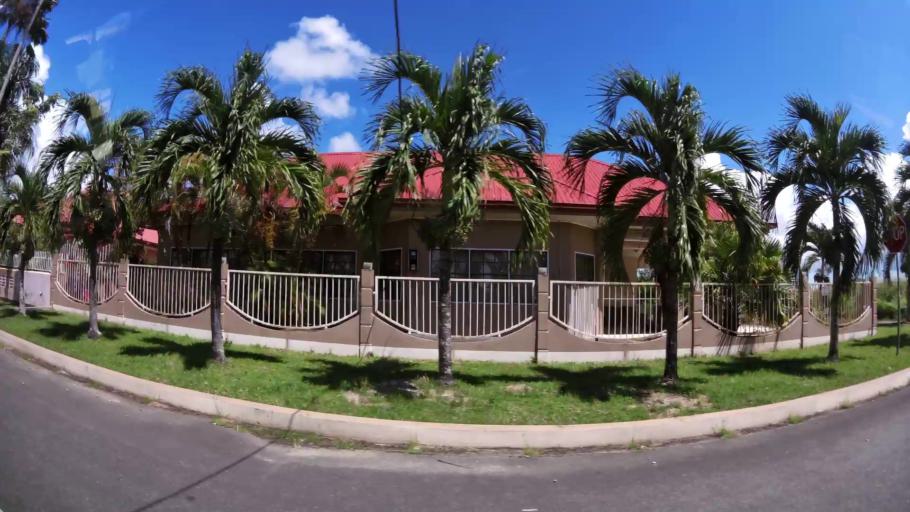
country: SR
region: Paramaribo
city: Paramaribo
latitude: 5.8659
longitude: -55.1427
